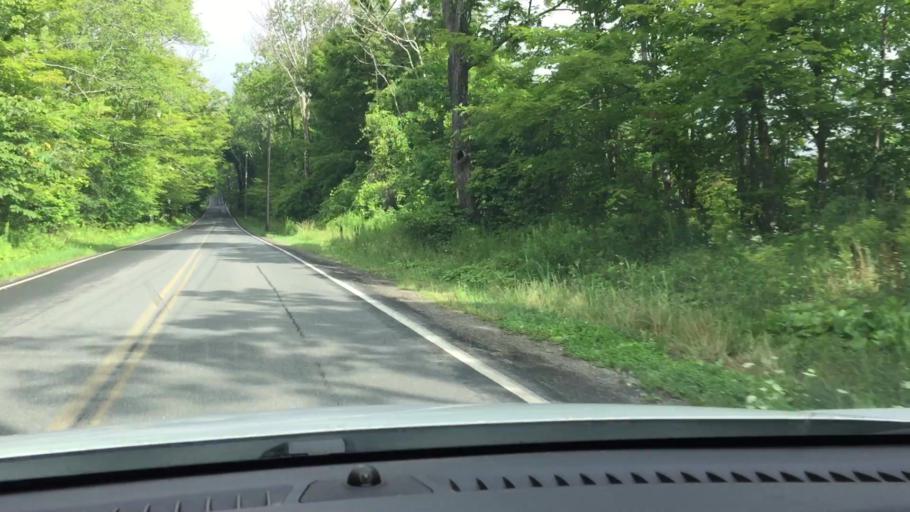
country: US
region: Massachusetts
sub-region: Berkshire County
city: Hinsdale
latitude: 42.4467
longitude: -73.1427
